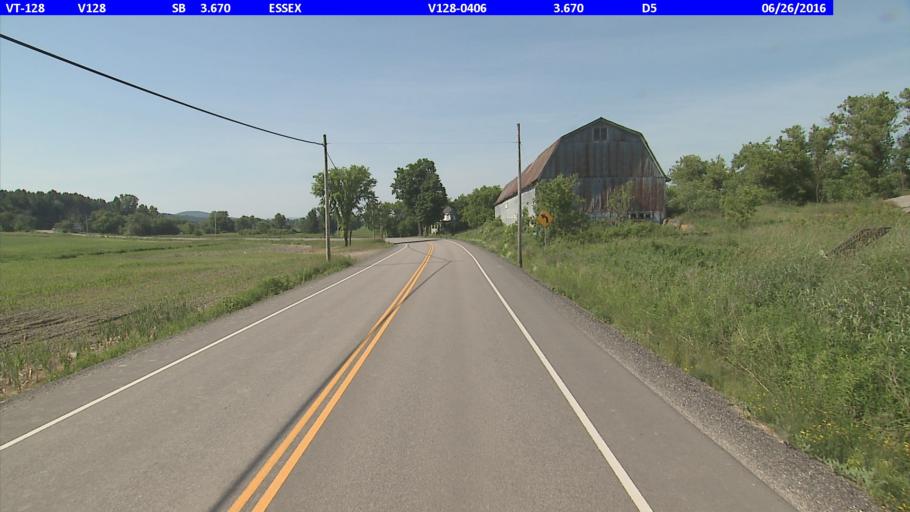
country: US
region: Vermont
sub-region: Chittenden County
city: Jericho
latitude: 44.5500
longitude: -73.0351
